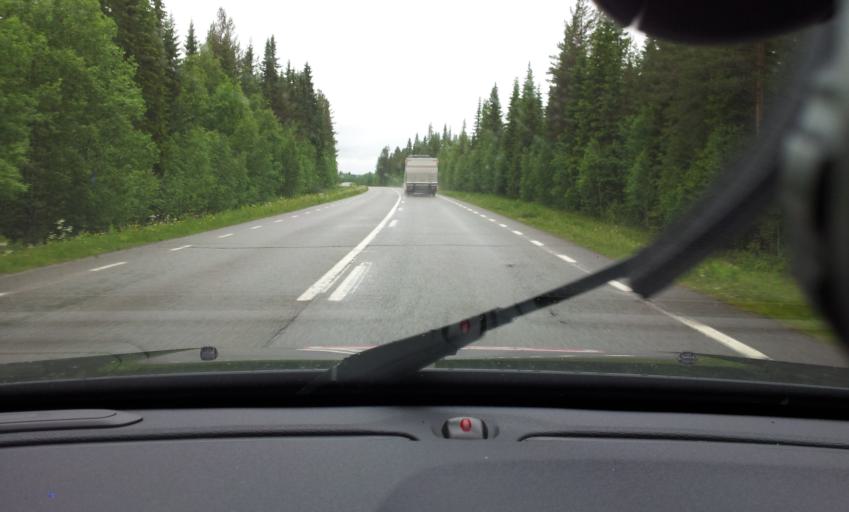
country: SE
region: Jaemtland
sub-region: OEstersunds Kommun
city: Lit
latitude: 63.6306
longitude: 14.6674
